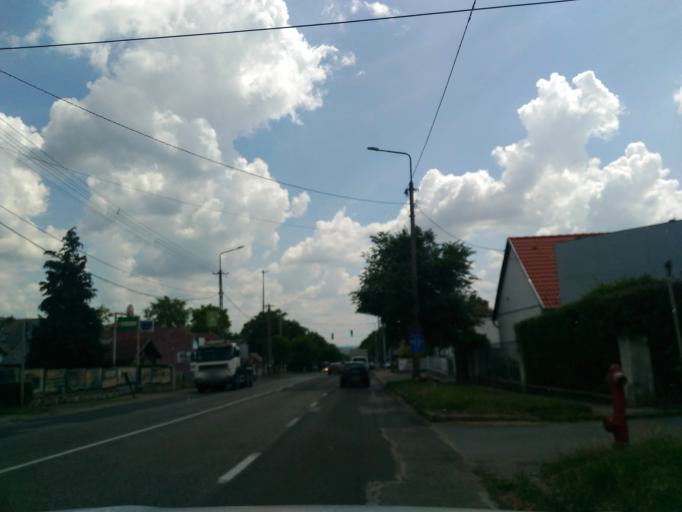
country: HU
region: Baranya
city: Pecs
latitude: 46.1036
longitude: 18.2646
